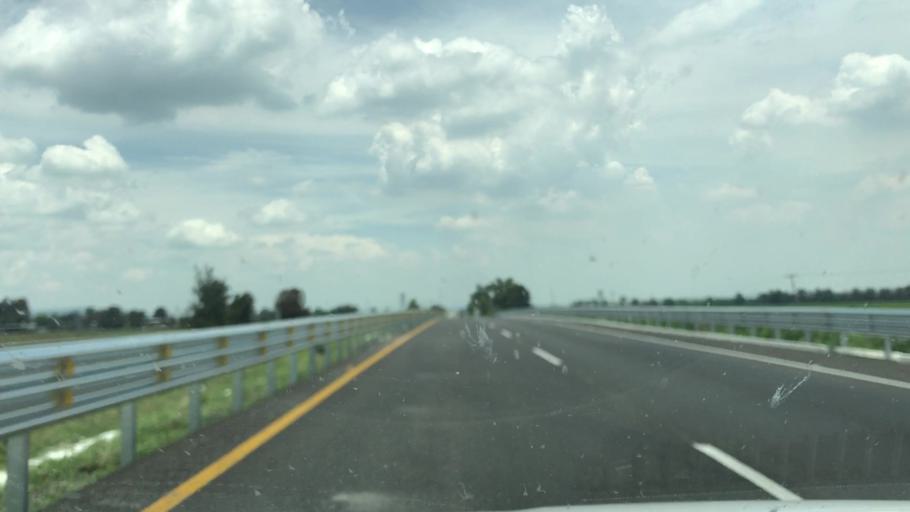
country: MX
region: Guanajuato
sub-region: Salamanca
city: San Vicente de Flores
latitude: 20.6307
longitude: -101.2502
